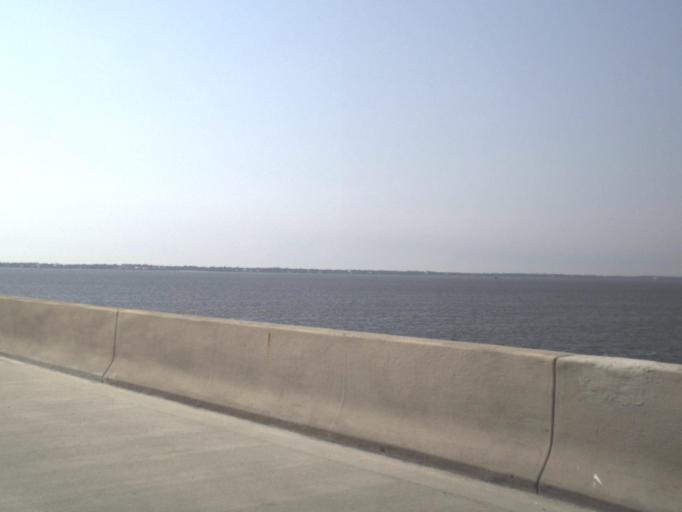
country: US
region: Florida
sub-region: Franklin County
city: Eastpoint
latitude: 29.6910
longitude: -84.8867
